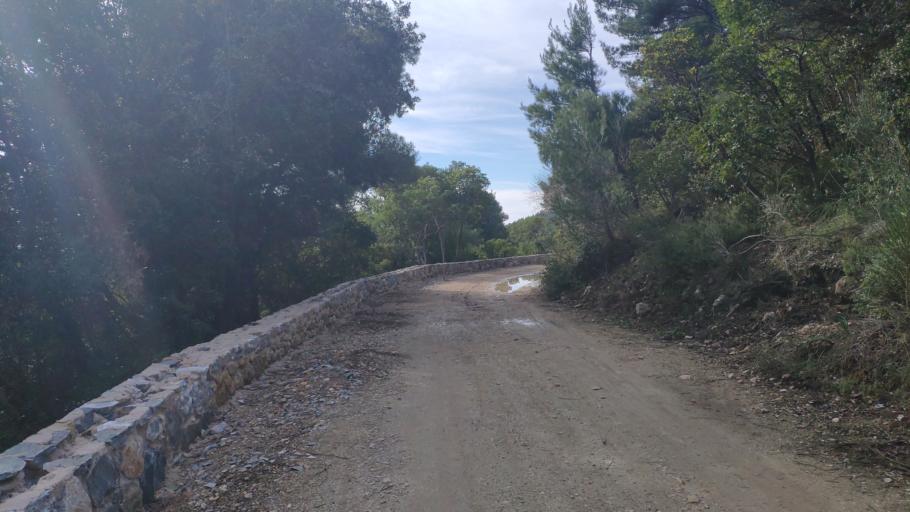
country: GR
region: Attica
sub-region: Nomarchia Anatolikis Attikis
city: Varybobi
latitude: 38.1654
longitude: 23.7800
